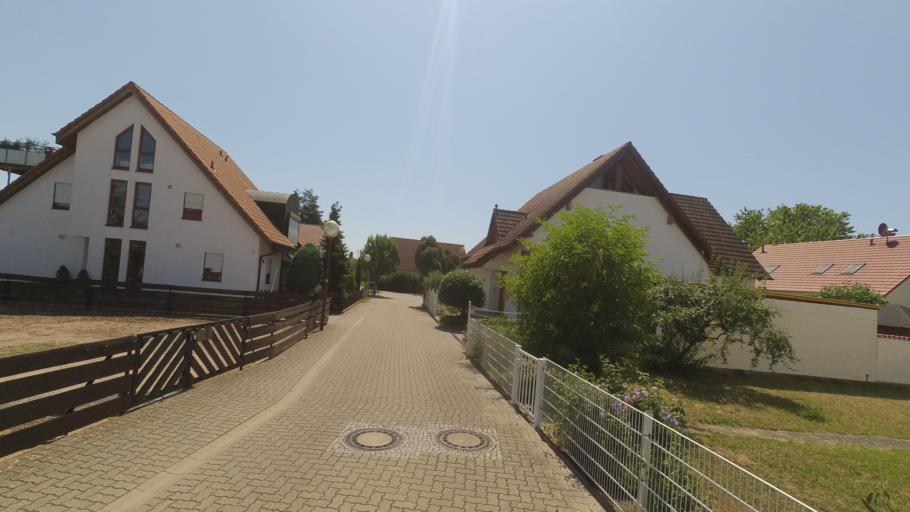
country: DE
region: Rheinland-Pfalz
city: Schifferstadt
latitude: 49.3966
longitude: 8.3731
